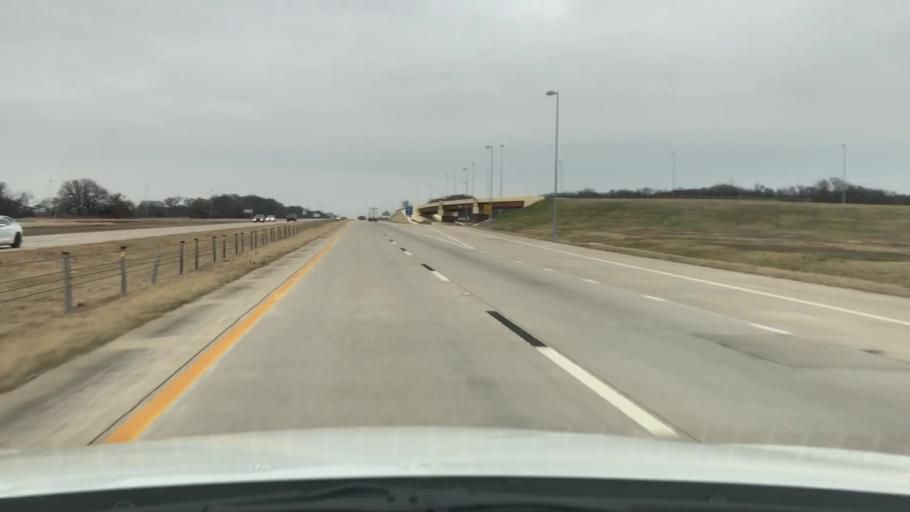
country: US
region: Texas
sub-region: Cooke County
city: Gainesville
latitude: 33.7665
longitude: -97.1348
